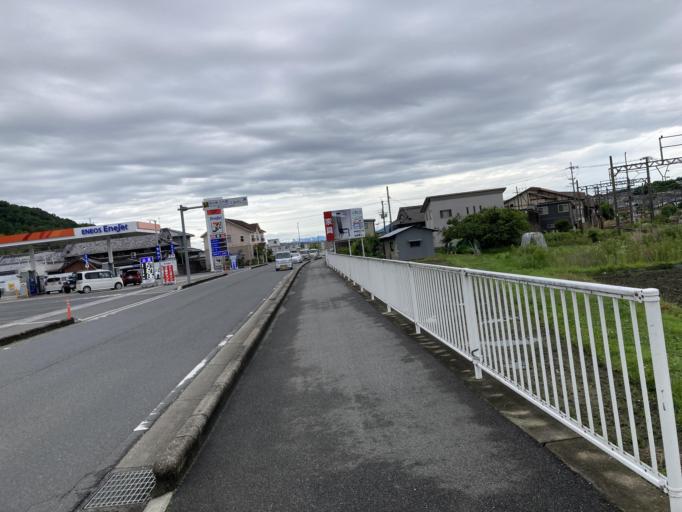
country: JP
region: Nara
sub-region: Ikoma-shi
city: Ikoma
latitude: 34.6251
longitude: 135.7069
